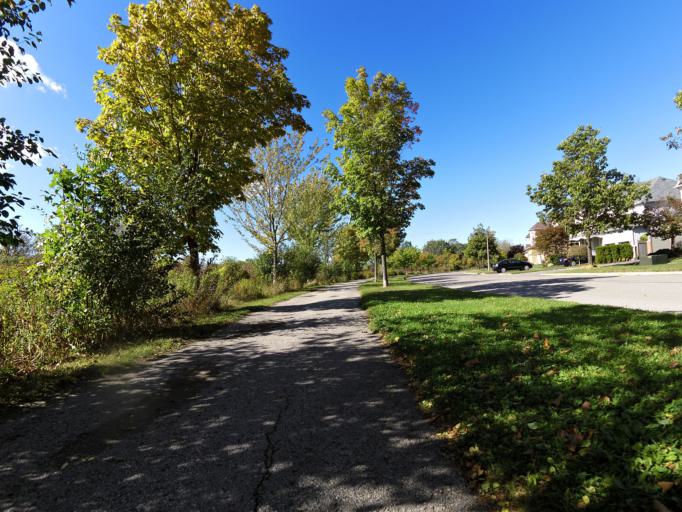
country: CA
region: Ontario
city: Ajax
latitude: 43.8509
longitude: -78.9566
